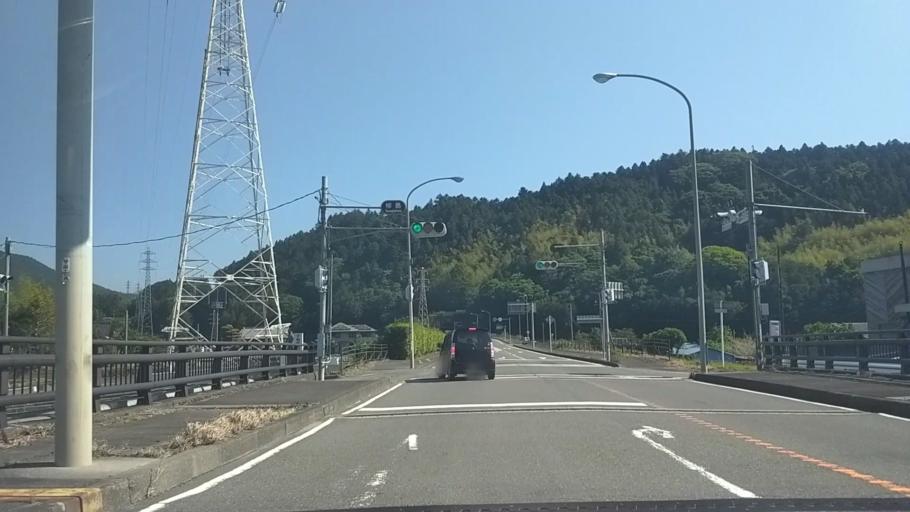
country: JP
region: Shizuoka
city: Fujinomiya
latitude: 35.2850
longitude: 138.4487
